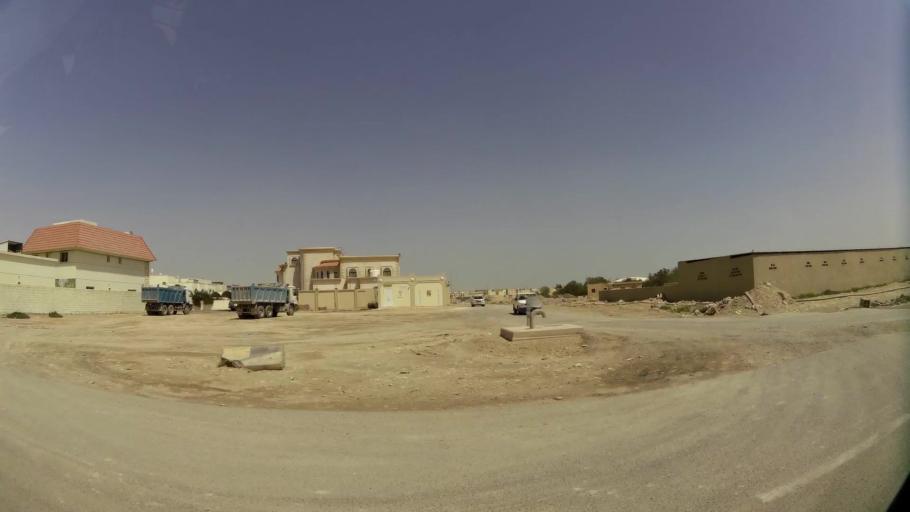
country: QA
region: Baladiyat Umm Salal
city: Umm Salal Muhammad
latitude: 25.3734
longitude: 51.4560
